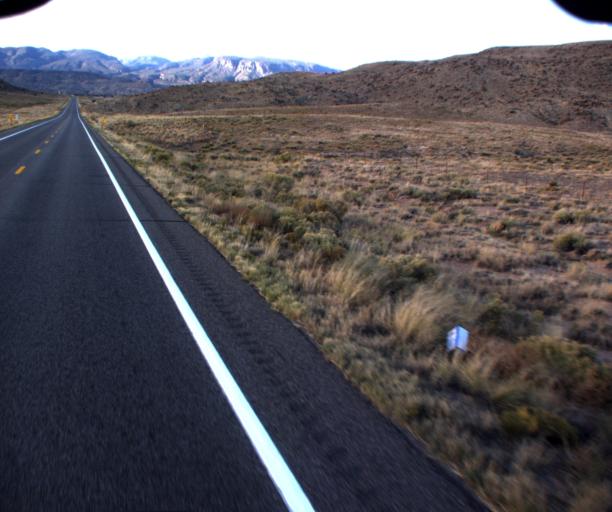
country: US
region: New Mexico
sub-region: San Juan County
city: Shiprock
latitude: 36.9418
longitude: -109.0752
